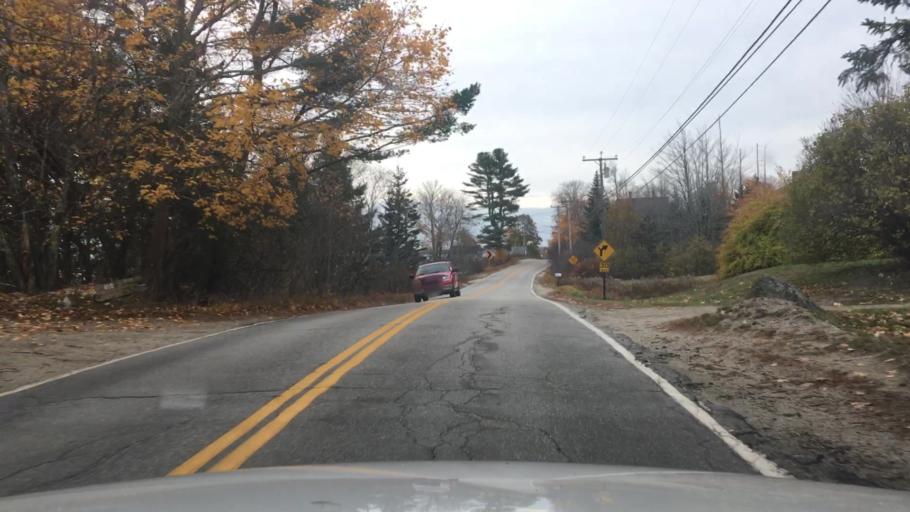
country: US
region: Maine
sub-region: Hancock County
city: Sedgwick
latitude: 44.3563
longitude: -68.5488
